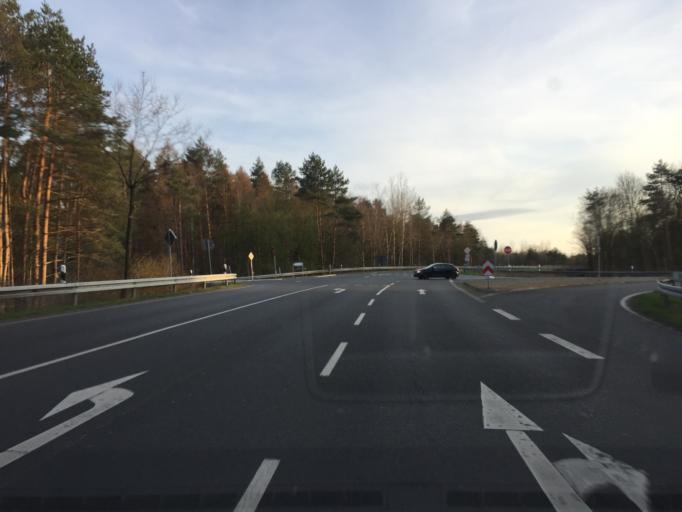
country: DE
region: Lower Saxony
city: Neustadt am Rubenberge
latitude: 52.4910
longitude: 9.4895
